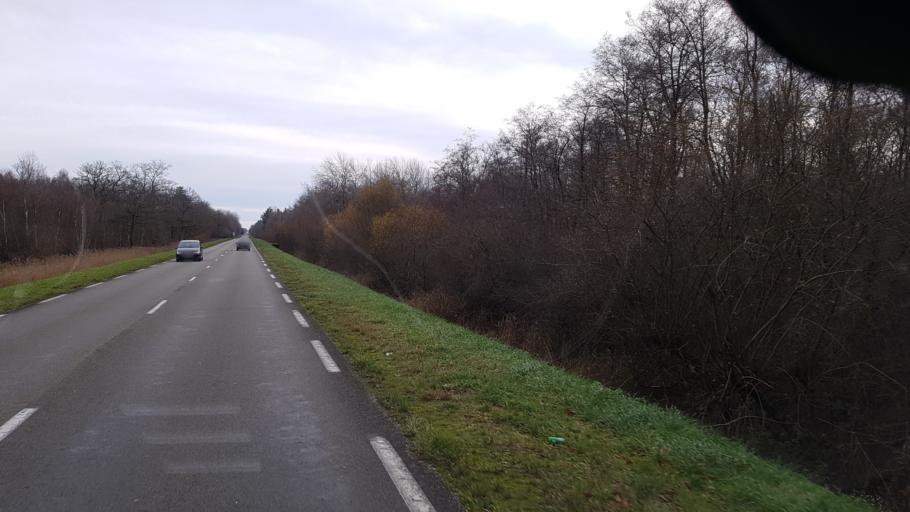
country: FR
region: Centre
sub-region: Departement du Loiret
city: La Ferte-Saint-Aubin
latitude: 47.6827
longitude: 1.9631
